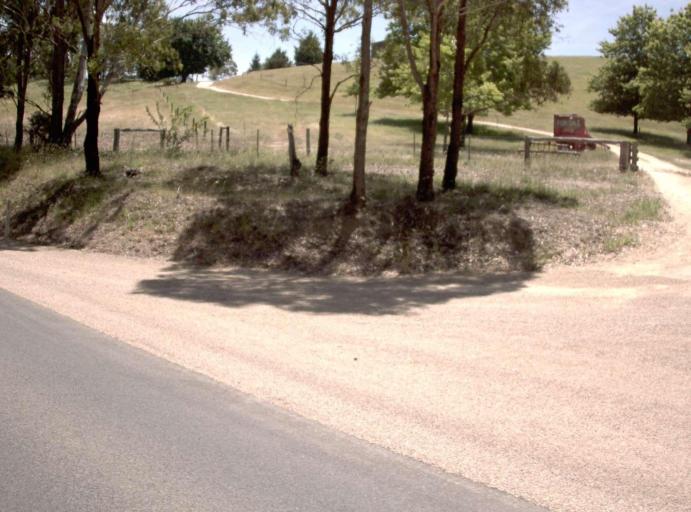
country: AU
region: Victoria
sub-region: East Gippsland
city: Bairnsdale
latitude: -37.7503
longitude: 147.7334
